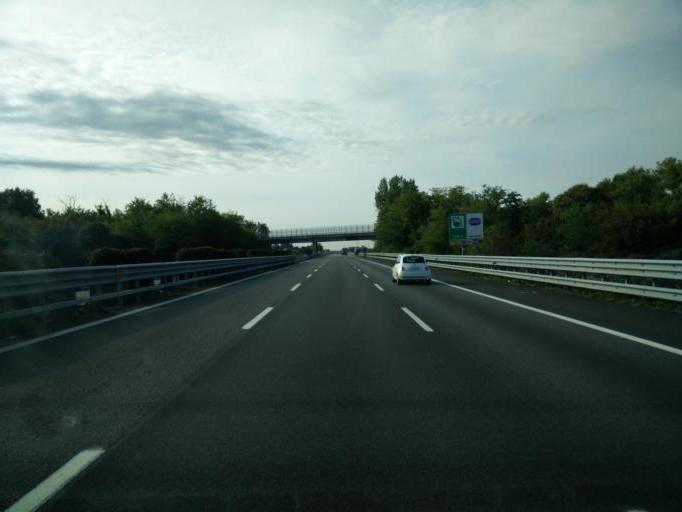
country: IT
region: Lombardy
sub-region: Provincia di Brescia
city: Montirone
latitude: 45.4565
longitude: 10.2148
